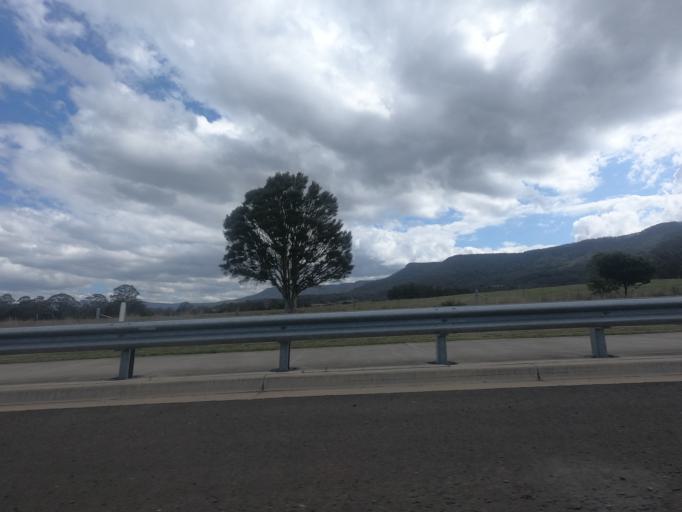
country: AU
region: New South Wales
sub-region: Wollongong
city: Dapto
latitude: -34.4812
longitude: 150.7660
